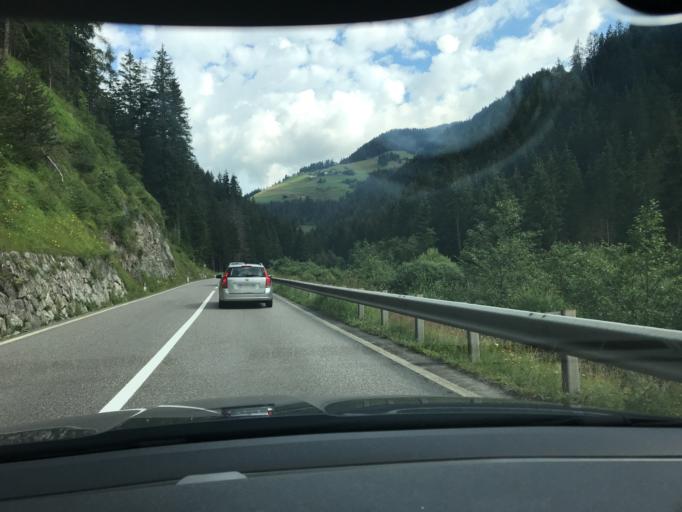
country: IT
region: Trentino-Alto Adige
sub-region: Bolzano
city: La Valle - Wengen
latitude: 46.6592
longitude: 11.9092
